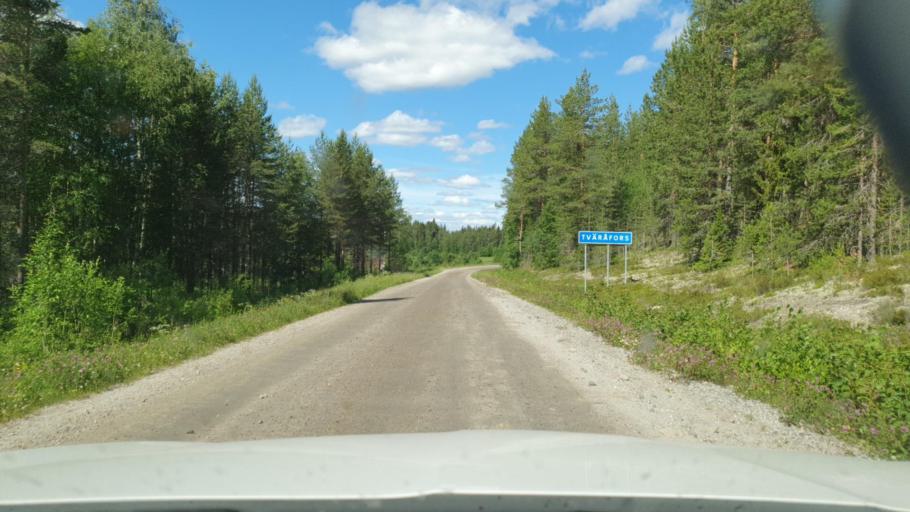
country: SE
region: Vaesterbotten
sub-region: Skelleftea Kommun
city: Backa
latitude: 65.1453
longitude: 21.1695
